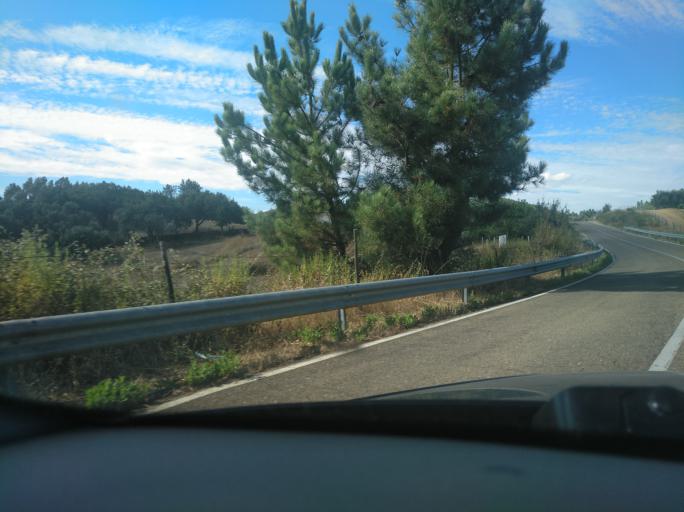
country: ES
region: Extremadura
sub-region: Provincia de Badajoz
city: La Codosera
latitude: 39.1807
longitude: -7.1763
